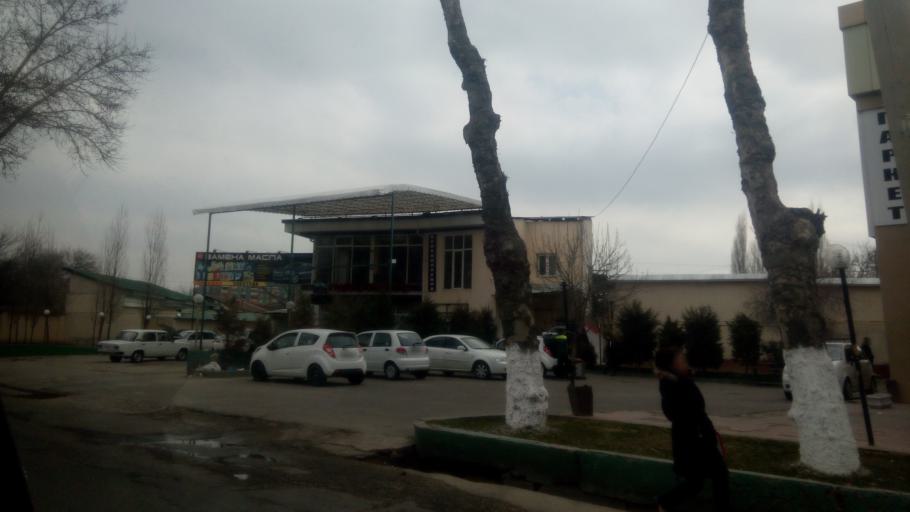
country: UZ
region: Toshkent Shahri
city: Tashkent
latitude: 41.3488
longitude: 69.2351
